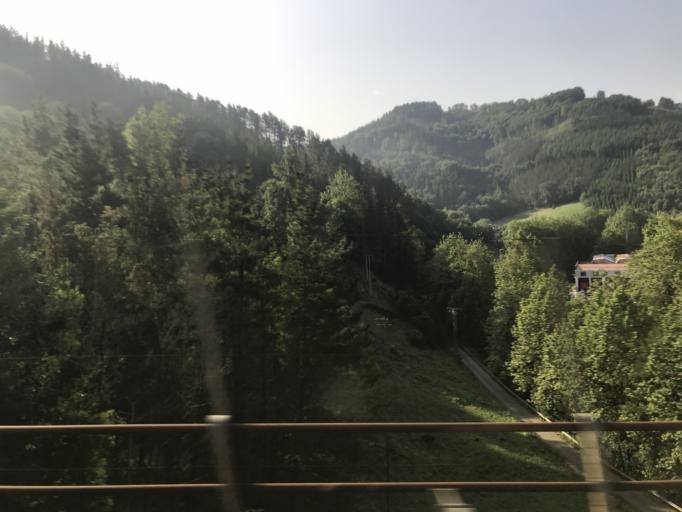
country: ES
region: Basque Country
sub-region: Provincia de Guipuzcoa
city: Icazteguieta
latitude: 43.0916
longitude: -2.1238
